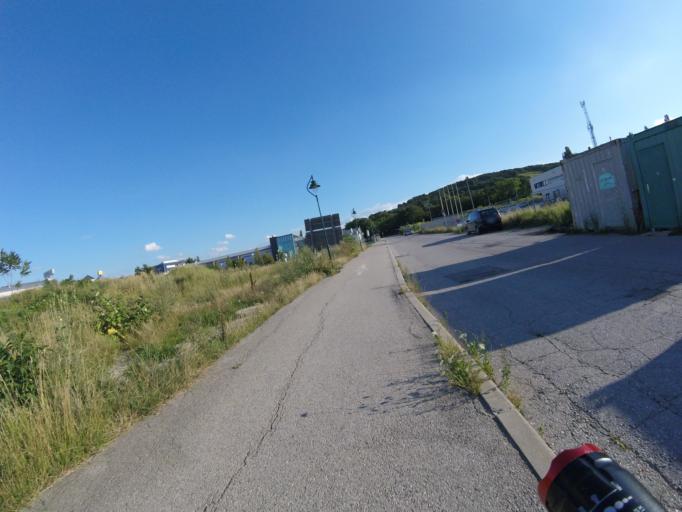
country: AT
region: Lower Austria
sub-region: Politischer Bezirk Modling
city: Neu-Guntramsdorf
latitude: 48.0719
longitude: 16.3023
